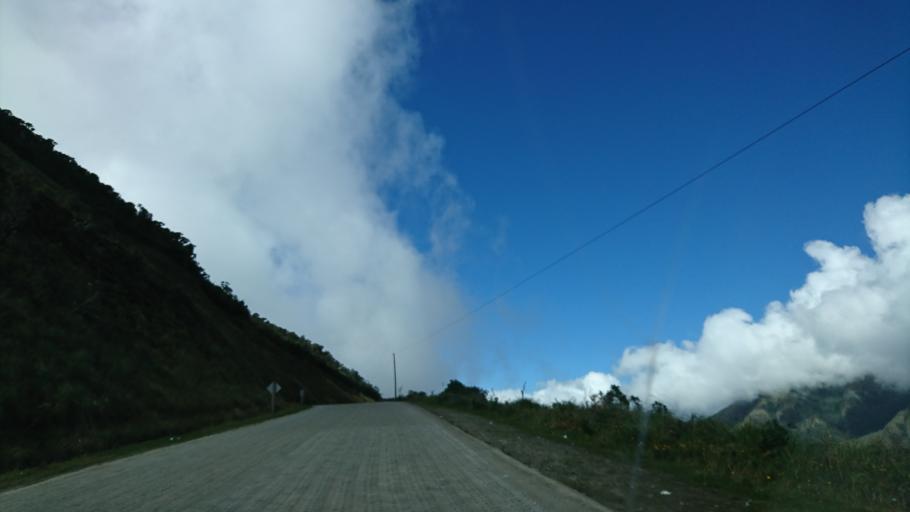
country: BO
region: La Paz
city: Coroico
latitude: -16.2896
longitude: -67.8750
